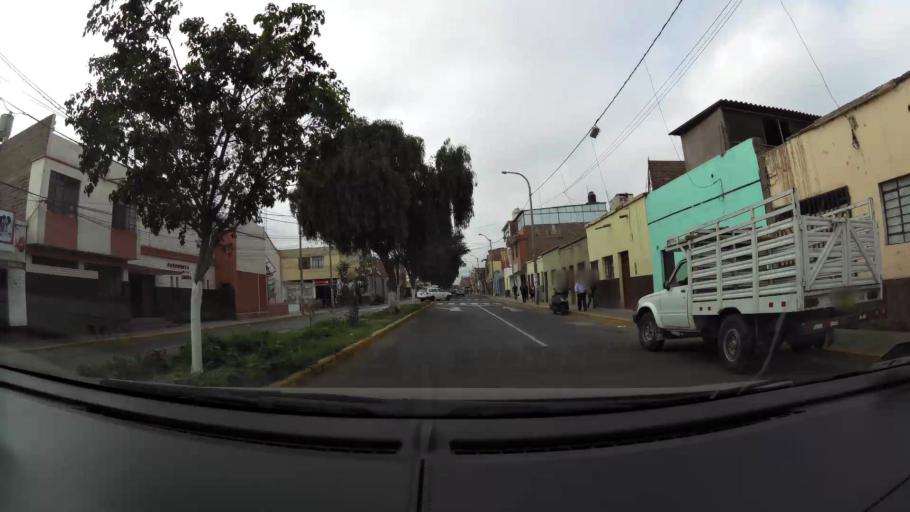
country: PE
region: La Libertad
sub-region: Provincia de Trujillo
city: Trujillo
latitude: -8.0993
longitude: -79.0169
